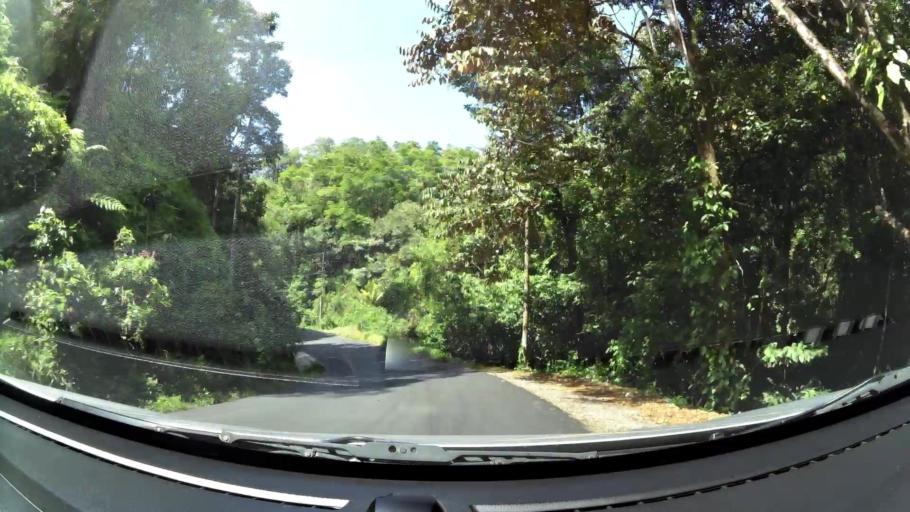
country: CR
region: San Jose
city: San Isidro
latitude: 9.2791
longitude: -83.8336
